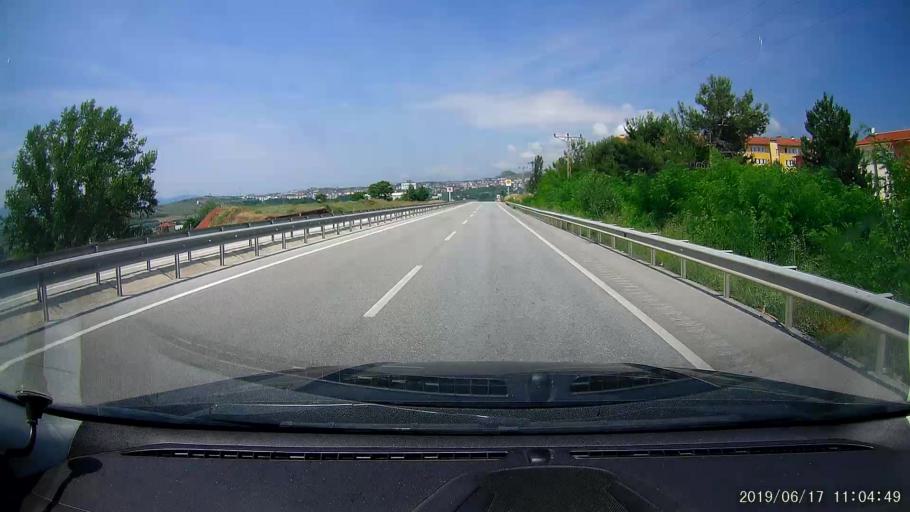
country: TR
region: Kastamonu
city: Tosya
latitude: 41.0191
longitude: 34.0860
